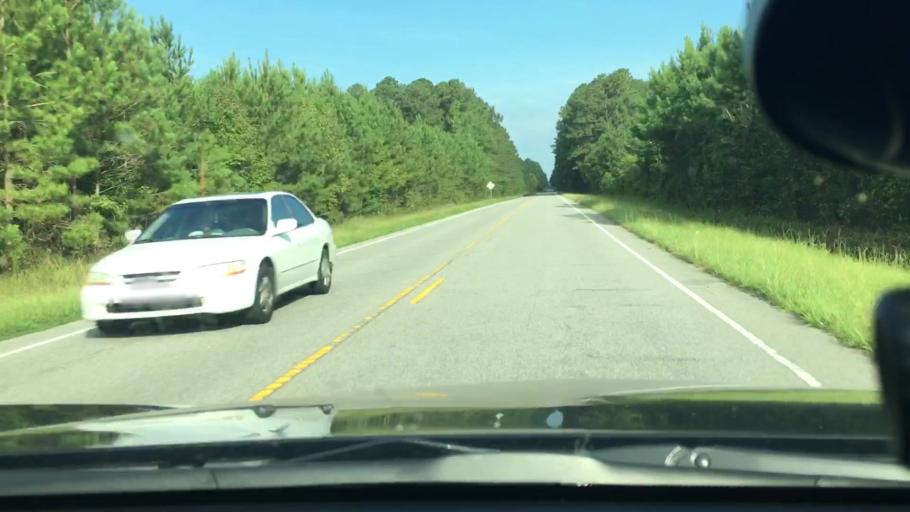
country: US
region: North Carolina
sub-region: Edgecombe County
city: Pinetops
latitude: 35.7619
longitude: -77.5586
